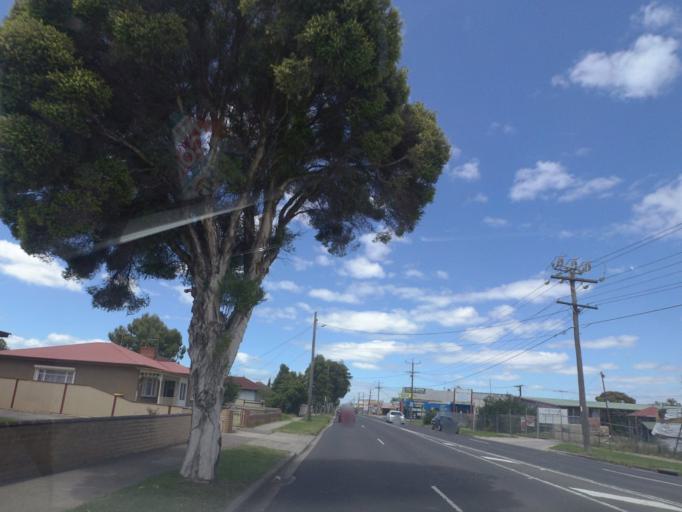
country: AU
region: Victoria
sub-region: Brimbank
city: Albion
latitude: -37.7660
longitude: 144.8309
